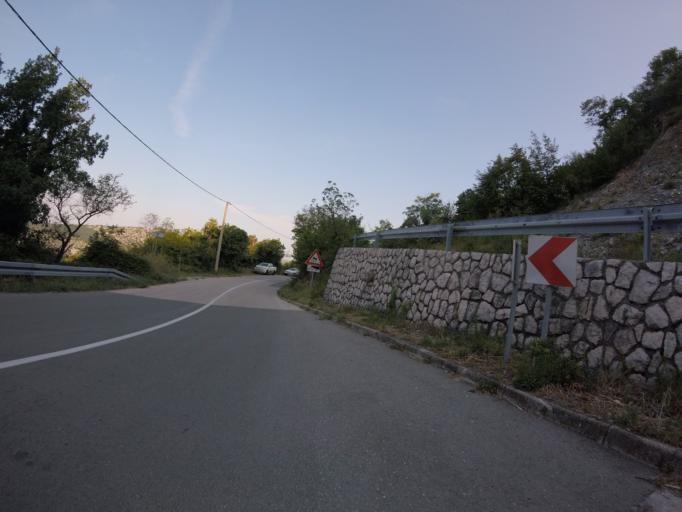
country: HR
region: Primorsko-Goranska
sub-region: Grad Crikvenica
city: Crikvenica
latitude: 45.1960
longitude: 14.7221
